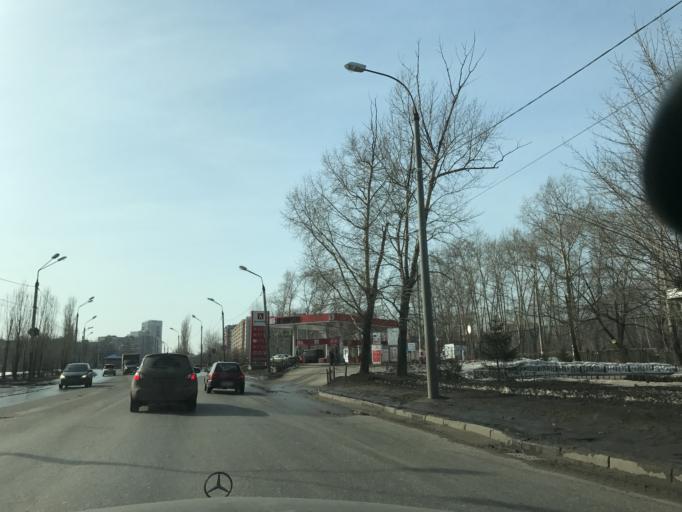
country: RU
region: Nizjnij Novgorod
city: Gorbatovka
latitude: 56.2634
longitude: 43.8680
